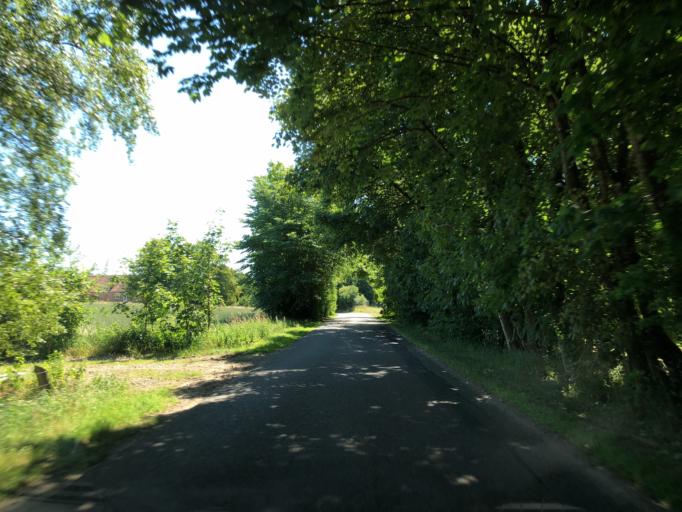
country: DK
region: Central Jutland
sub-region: Viborg Kommune
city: Viborg
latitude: 56.5178
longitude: 9.4916
